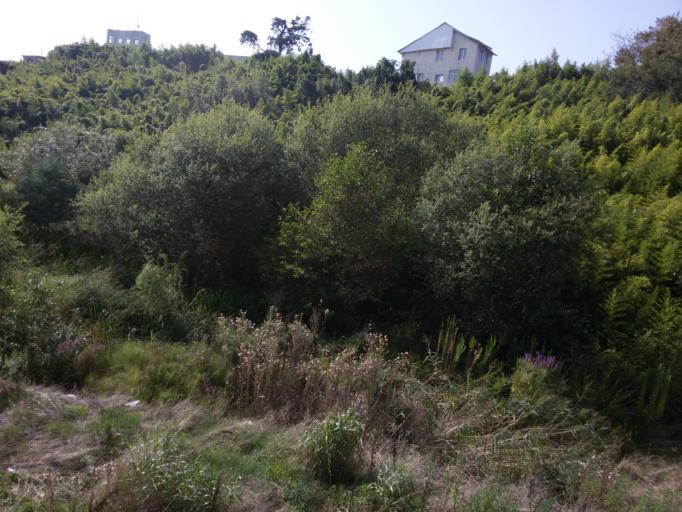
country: RU
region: Krasnodarskiy
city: Adler
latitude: 43.4183
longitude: 39.9406
